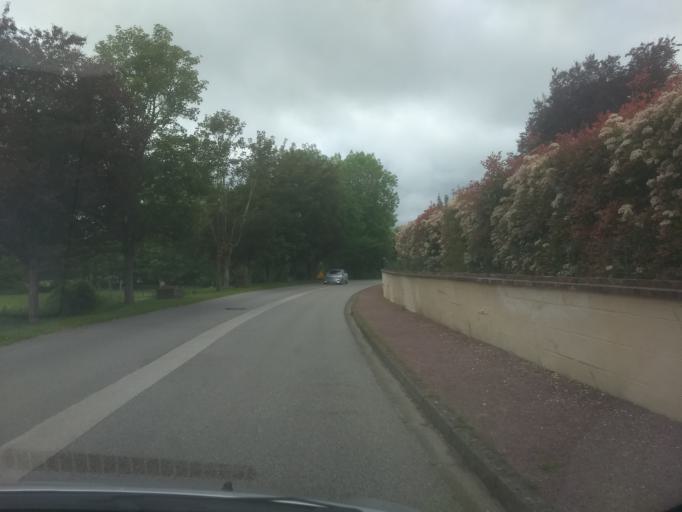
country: FR
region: Lower Normandy
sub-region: Departement de l'Orne
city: Bretoncelles
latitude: 48.4762
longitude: 0.8488
